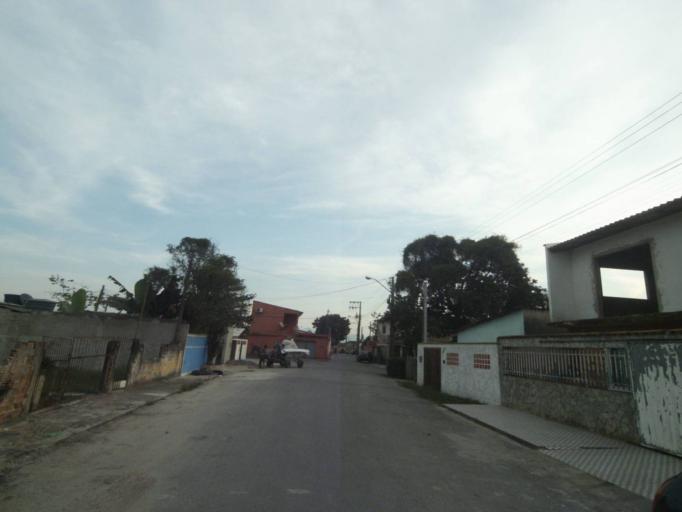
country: BR
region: Parana
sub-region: Paranagua
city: Paranagua
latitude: -25.5265
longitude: -48.5309
